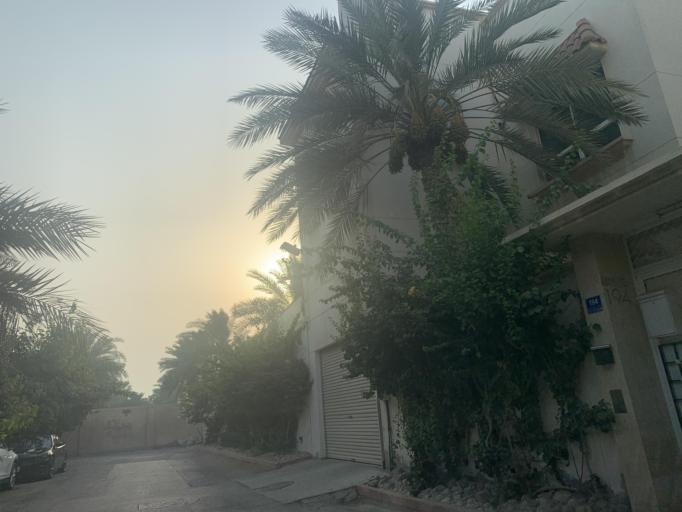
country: BH
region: Manama
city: Jidd Hafs
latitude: 26.2247
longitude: 50.5168
